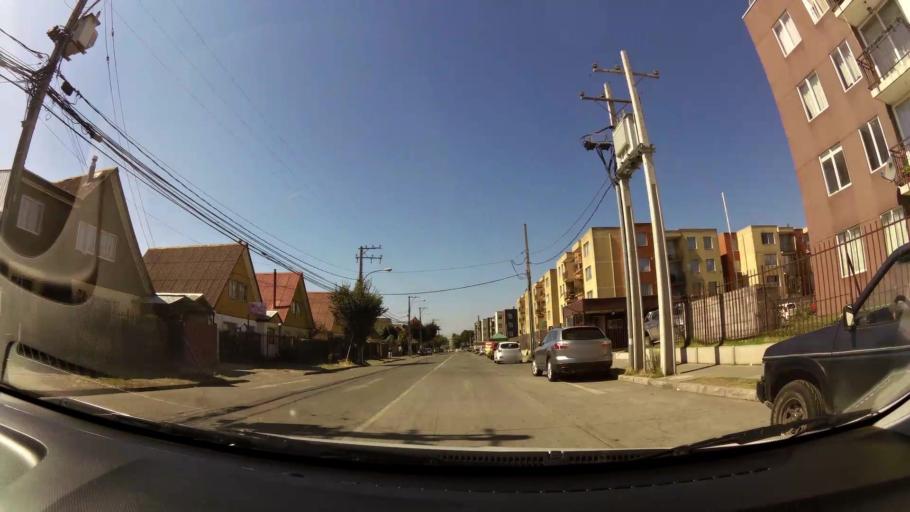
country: CL
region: Biobio
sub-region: Provincia de Concepcion
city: Concepcion
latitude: -36.7918
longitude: -73.0362
